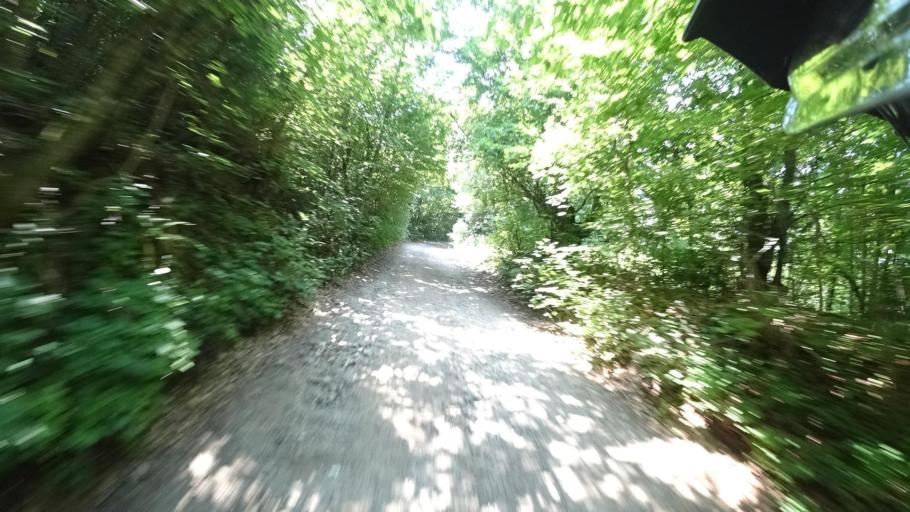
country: HR
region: Primorsko-Goranska
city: Vrbovsko
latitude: 45.3068
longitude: 15.1399
